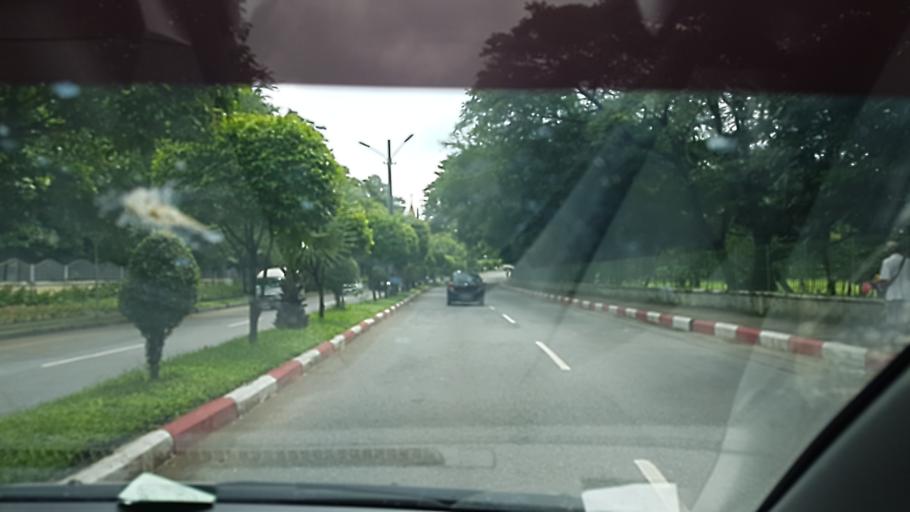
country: MM
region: Yangon
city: Yangon
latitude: 16.7950
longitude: 96.1479
